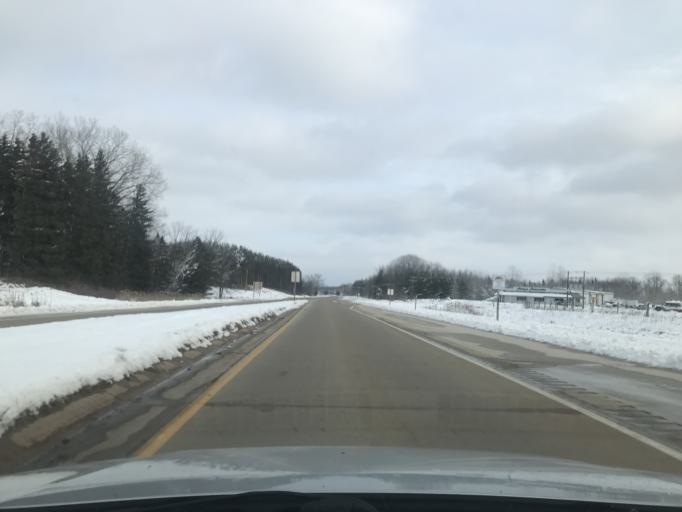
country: US
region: Wisconsin
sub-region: Oconto County
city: Oconto Falls
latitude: 44.8868
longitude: -88.0410
